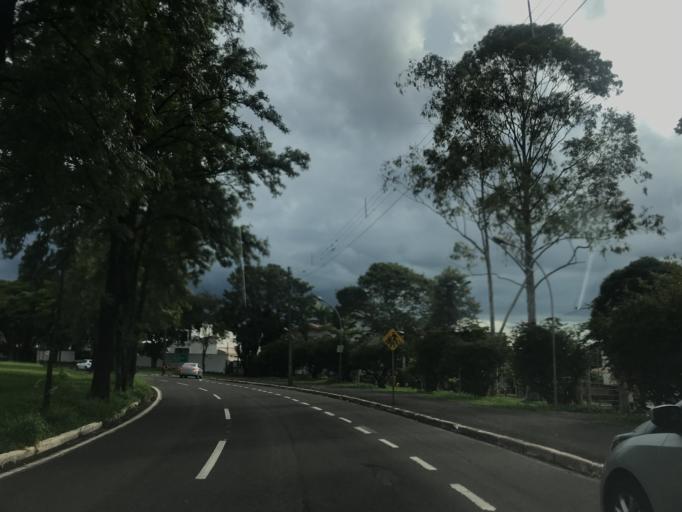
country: BR
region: Parana
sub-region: Maringa
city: Maringa
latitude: -23.4283
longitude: -51.9608
